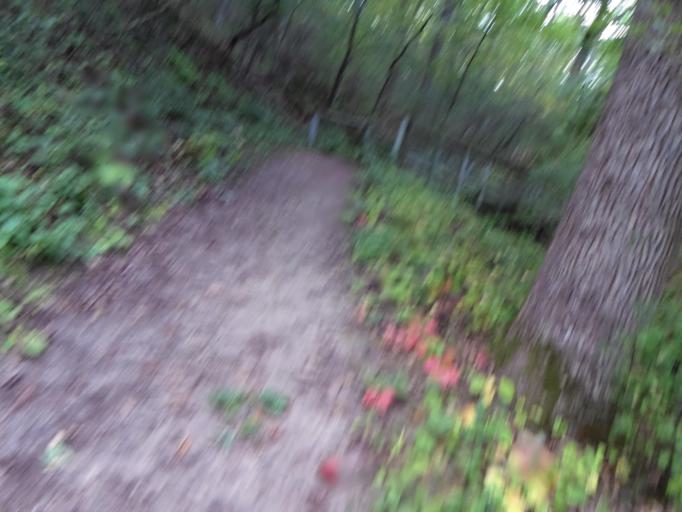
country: US
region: Minnesota
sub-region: Washington County
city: Afton
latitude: 44.8588
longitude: -92.7946
